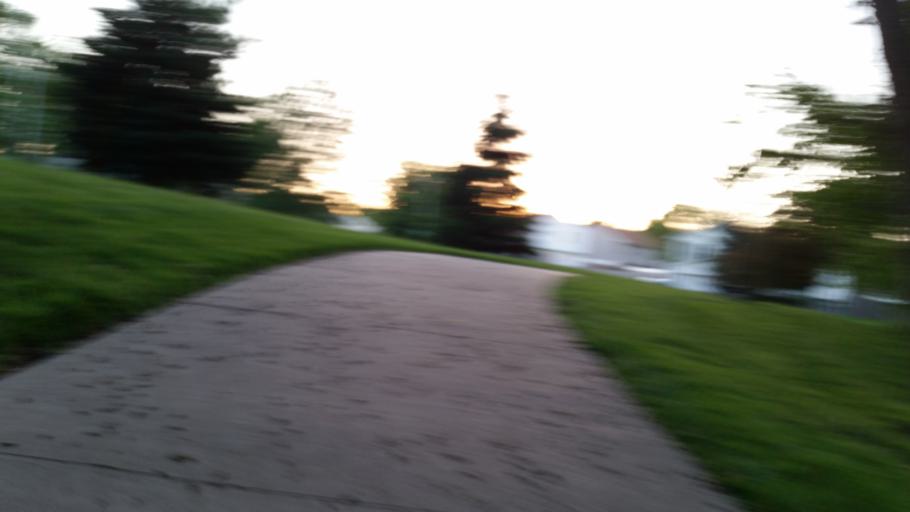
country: US
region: Nebraska
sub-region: Sarpy County
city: Offutt Air Force Base
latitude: 41.1083
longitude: -95.9560
